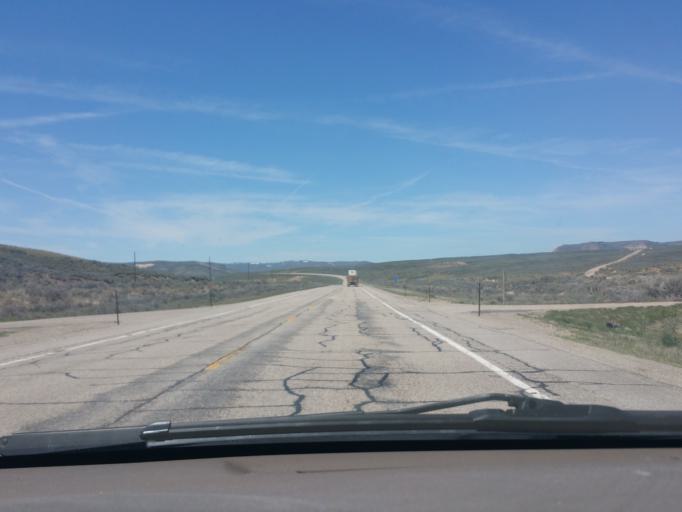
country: US
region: Wyoming
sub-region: Lincoln County
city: Kemmerer
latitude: 41.8159
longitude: -110.6520
